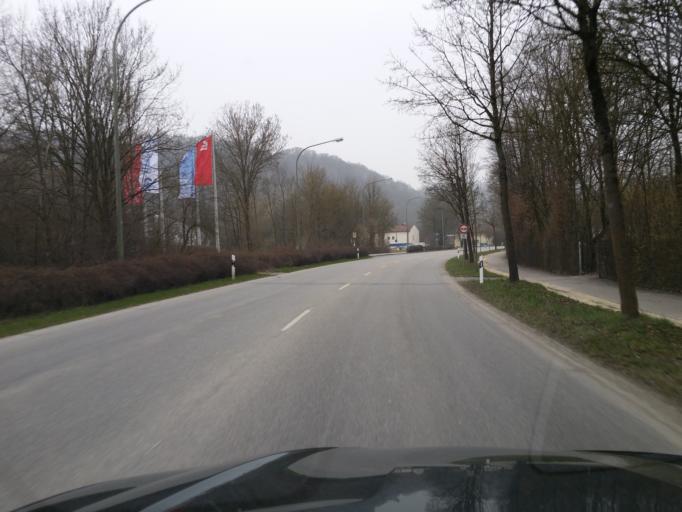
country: DE
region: Bavaria
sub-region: Lower Bavaria
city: Stallwang
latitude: 48.5571
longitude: 12.2007
